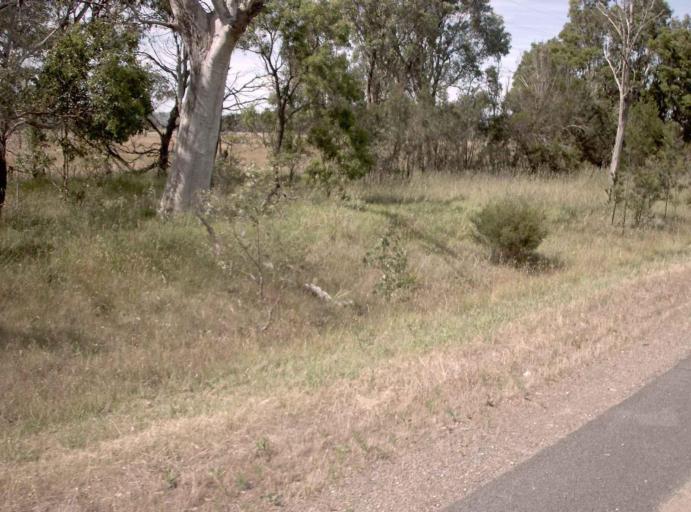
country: AU
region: Victoria
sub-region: East Gippsland
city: Bairnsdale
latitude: -37.8586
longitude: 147.5243
